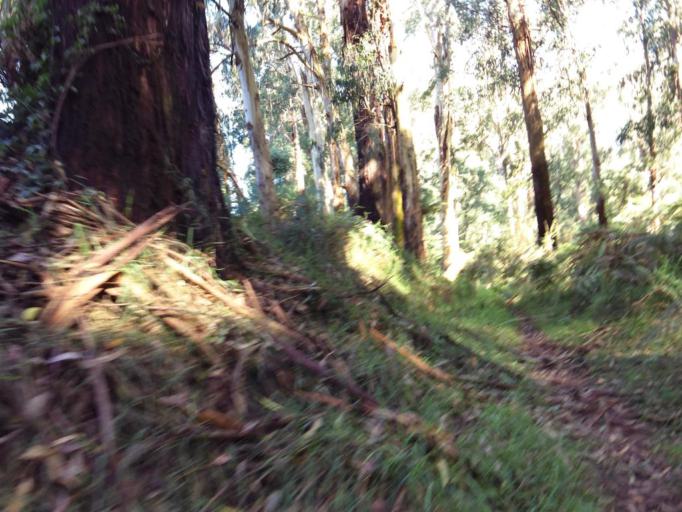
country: AU
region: Victoria
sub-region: Cardinia
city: Emerald
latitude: -37.9118
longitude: 145.4398
